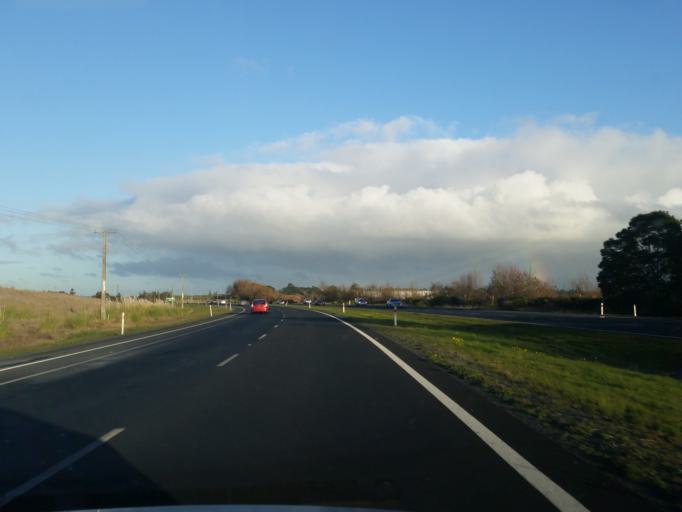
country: NZ
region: Waikato
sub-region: Waikato District
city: Te Kauwhata
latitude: -37.3017
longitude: 175.0616
